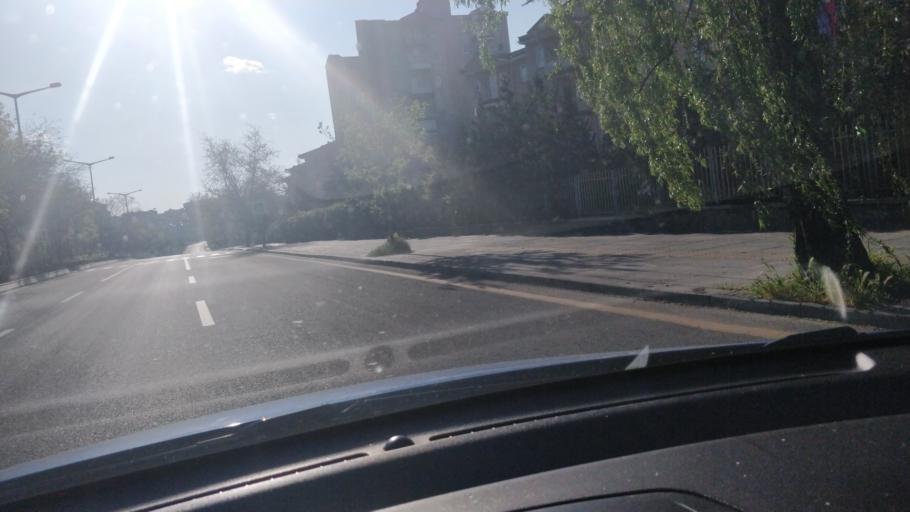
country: TR
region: Ankara
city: Batikent
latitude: 39.9581
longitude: 32.7278
